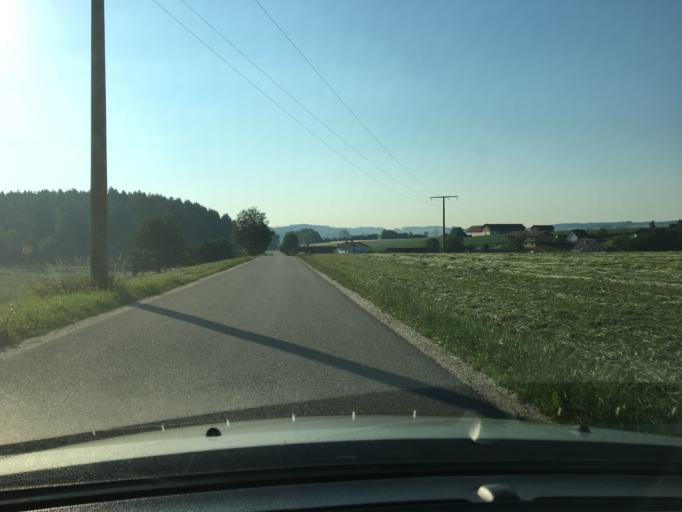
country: DE
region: Bavaria
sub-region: Lower Bavaria
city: Vilsbiburg
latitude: 48.4398
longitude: 12.3247
